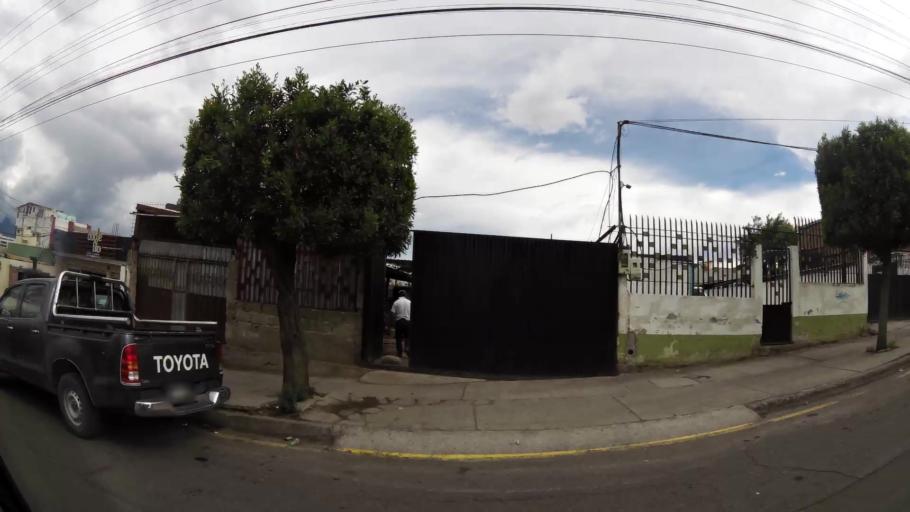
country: EC
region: Tungurahua
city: Ambato
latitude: -1.2660
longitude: -78.6309
